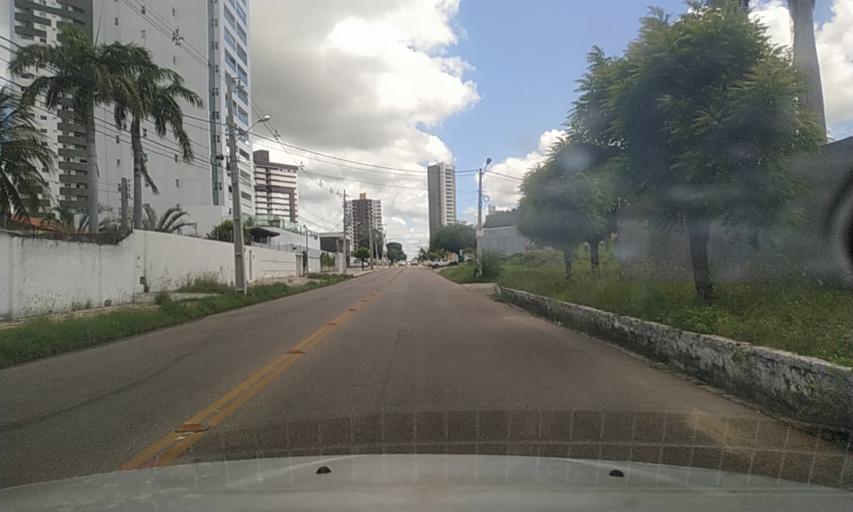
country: BR
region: Rio Grande do Norte
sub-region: Mossoro
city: Mossoro
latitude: -5.1811
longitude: -37.3585
